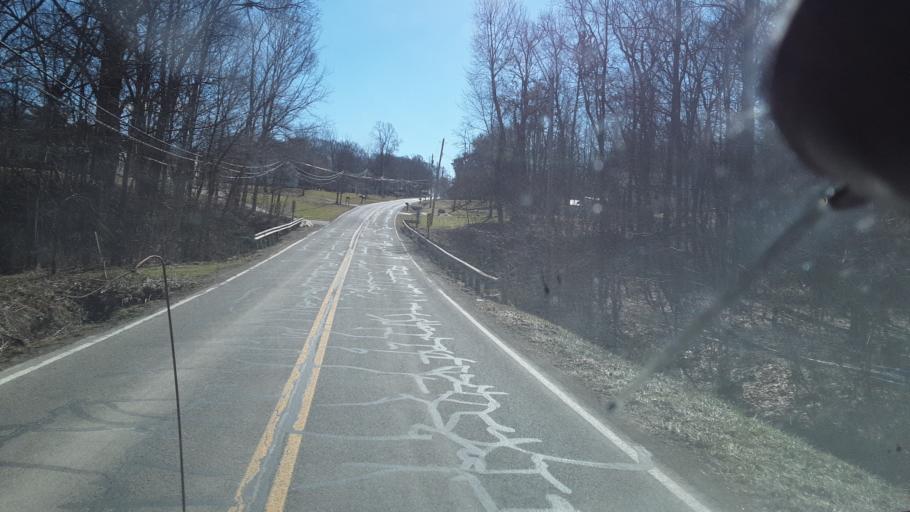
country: US
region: Ohio
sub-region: Richland County
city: Mansfield
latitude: 40.7404
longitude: -82.4940
